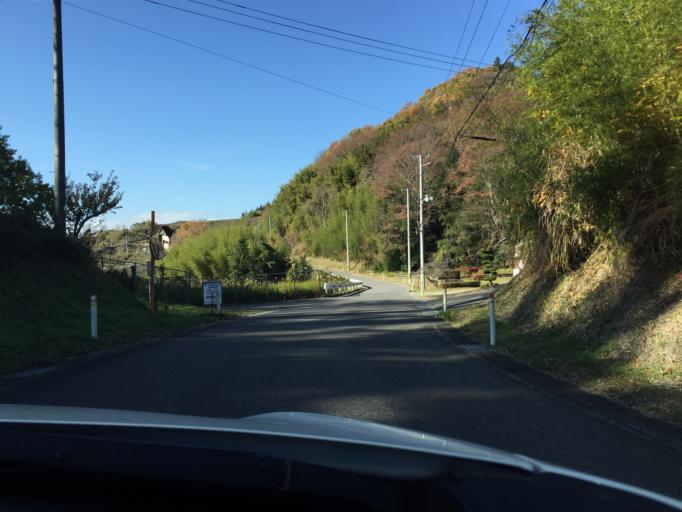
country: JP
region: Fukushima
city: Miharu
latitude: 37.4145
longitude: 140.4952
